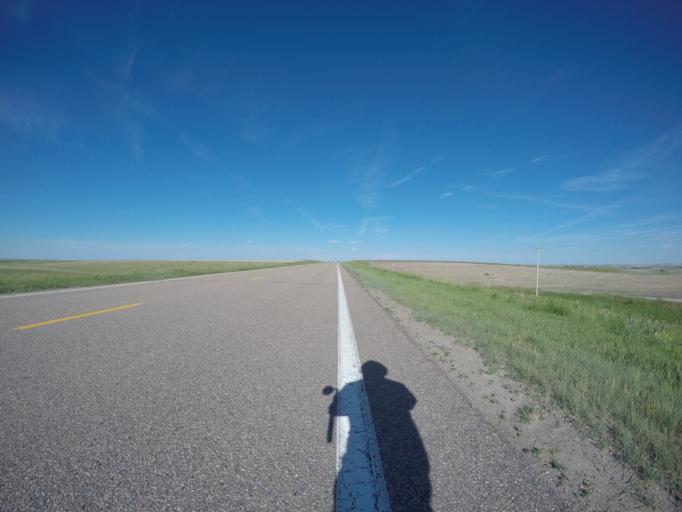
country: US
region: Kansas
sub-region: Cheyenne County
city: Saint Francis
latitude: 39.7566
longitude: -101.9523
